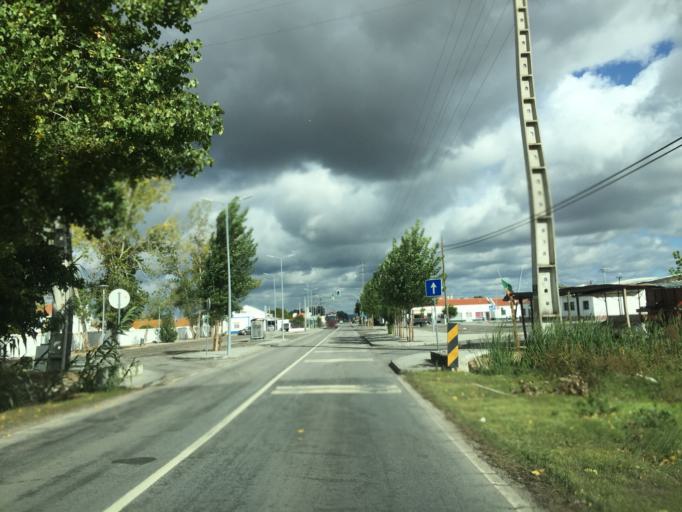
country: PT
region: Santarem
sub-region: Coruche
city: Coruche
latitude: 38.9534
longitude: -8.4941
